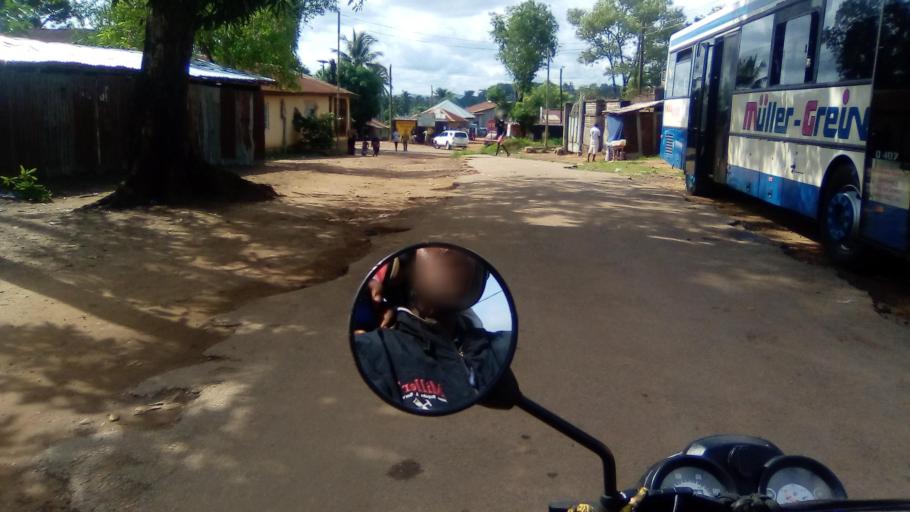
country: SL
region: Southern Province
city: Bo
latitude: 7.9558
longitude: -11.7533
